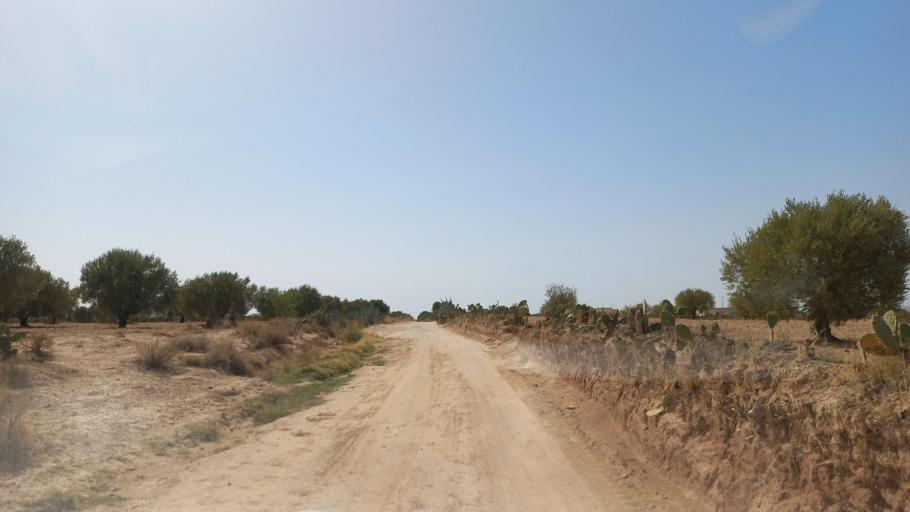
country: TN
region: Al Qasrayn
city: Kasserine
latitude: 35.2178
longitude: 9.0378
